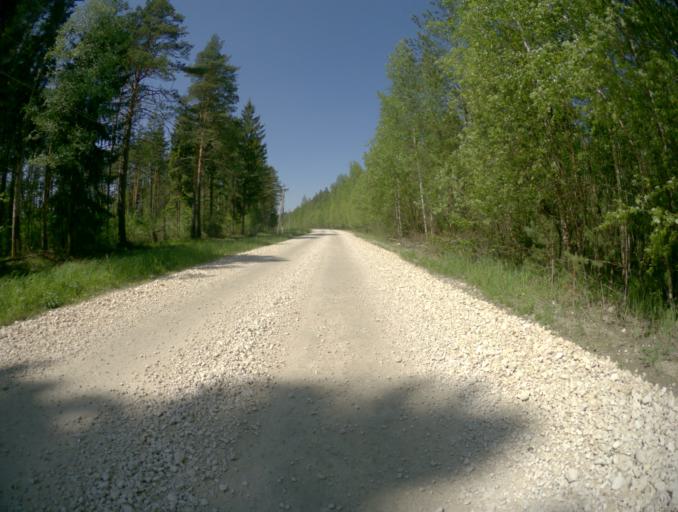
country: RU
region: Vladimir
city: Gusevskiy
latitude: 55.7216
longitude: 40.5765
